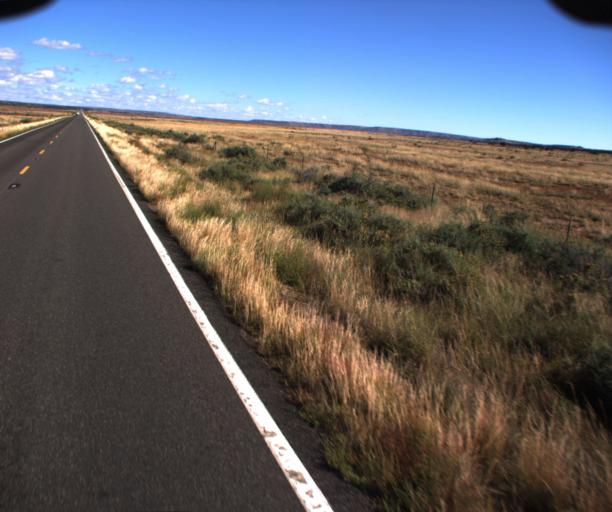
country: US
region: Arizona
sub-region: Apache County
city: Saint Johns
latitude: 34.6849
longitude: -109.2799
